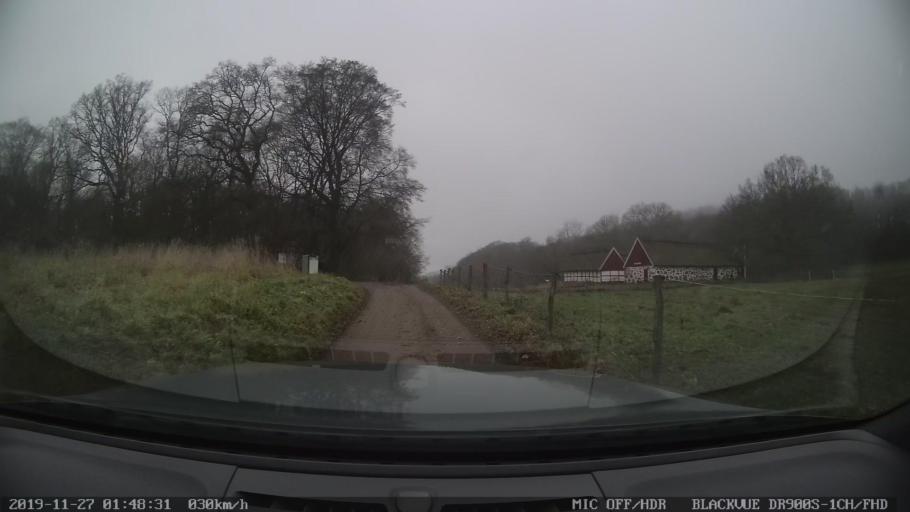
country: SE
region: Skane
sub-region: Hoganas Kommun
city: Hoganas
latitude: 56.2797
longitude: 12.5442
